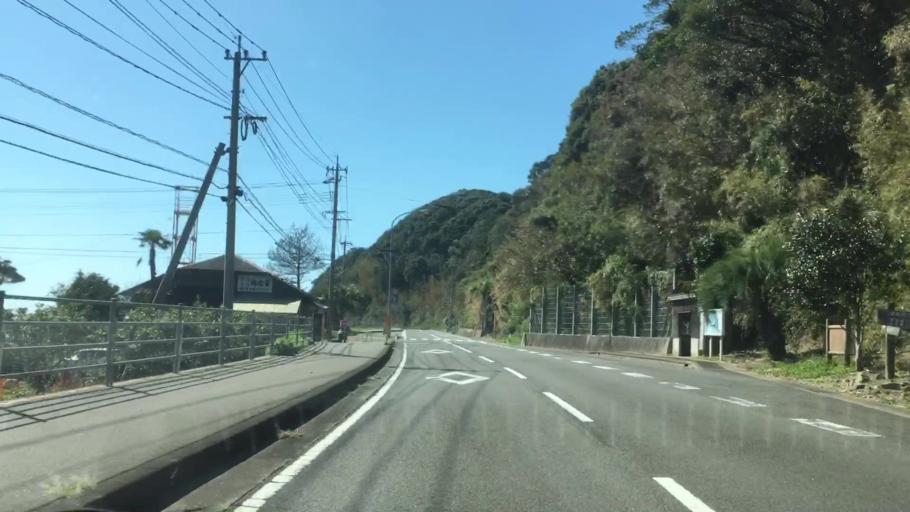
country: JP
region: Nagasaki
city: Sasebo
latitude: 33.0294
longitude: 129.6024
